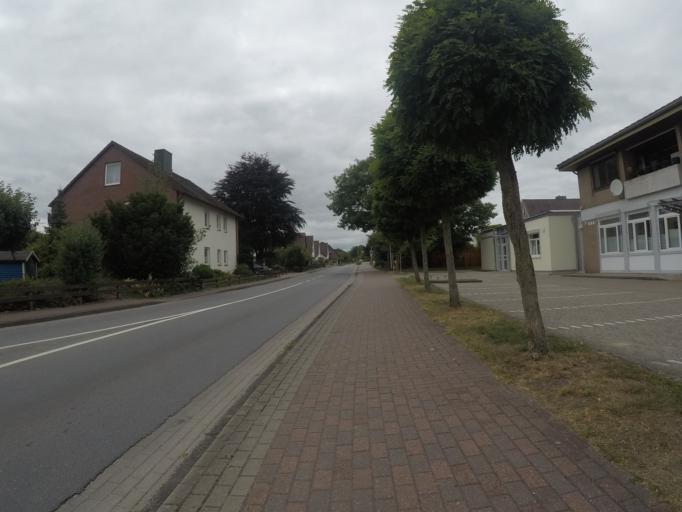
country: DE
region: Lower Saxony
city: Hemmoor
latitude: 53.6886
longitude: 9.1522
